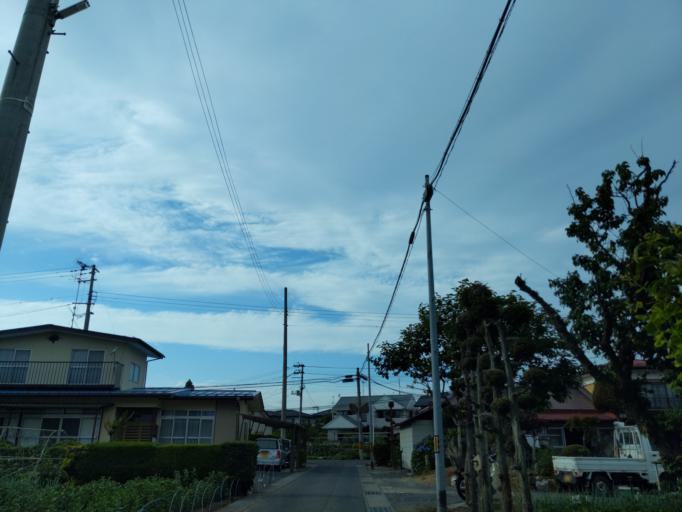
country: JP
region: Fukushima
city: Koriyama
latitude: 37.4143
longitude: 140.3534
